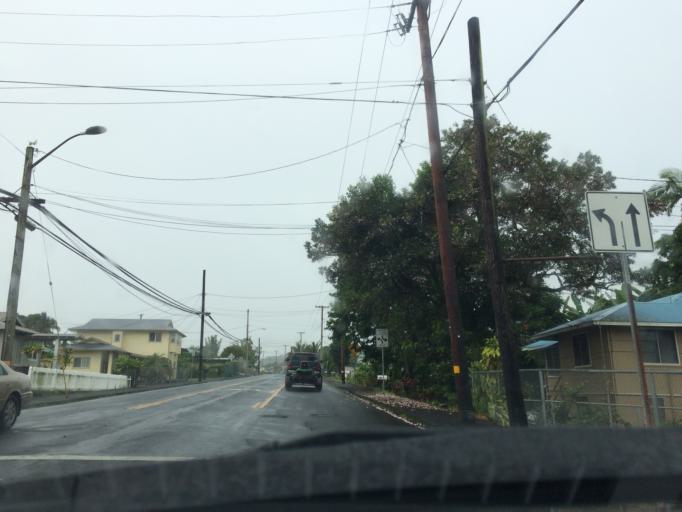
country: US
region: Hawaii
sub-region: Hawaii County
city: Hilo
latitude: 19.7150
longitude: -155.1048
